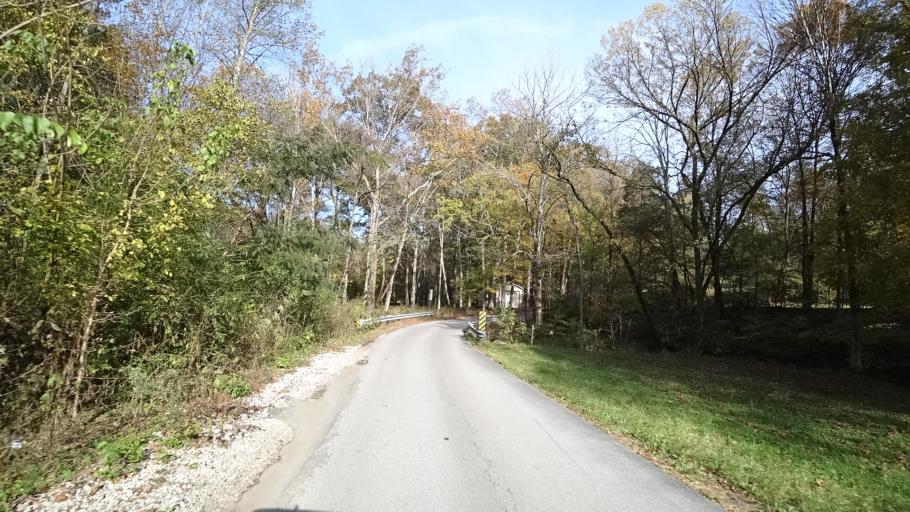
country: US
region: Tennessee
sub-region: Knox County
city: Farragut
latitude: 35.9149
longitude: -84.1750
